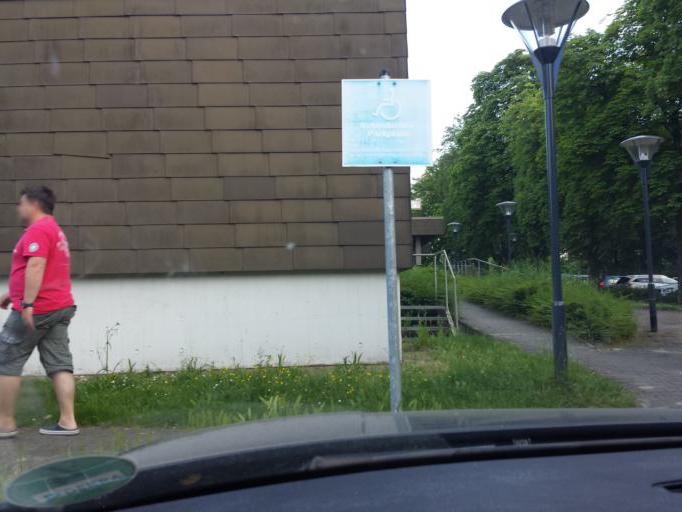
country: DE
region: Berlin
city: Mariendorf
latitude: 52.4341
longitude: 13.4050
